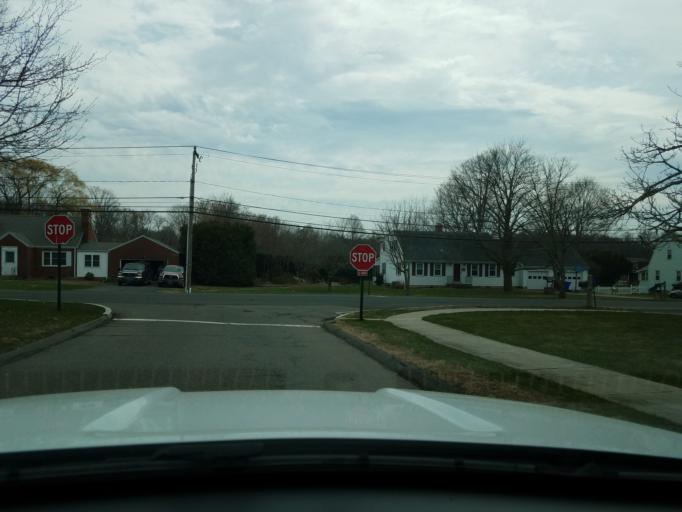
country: US
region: Connecticut
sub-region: Hartford County
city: Newington
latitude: 41.6492
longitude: -72.6850
